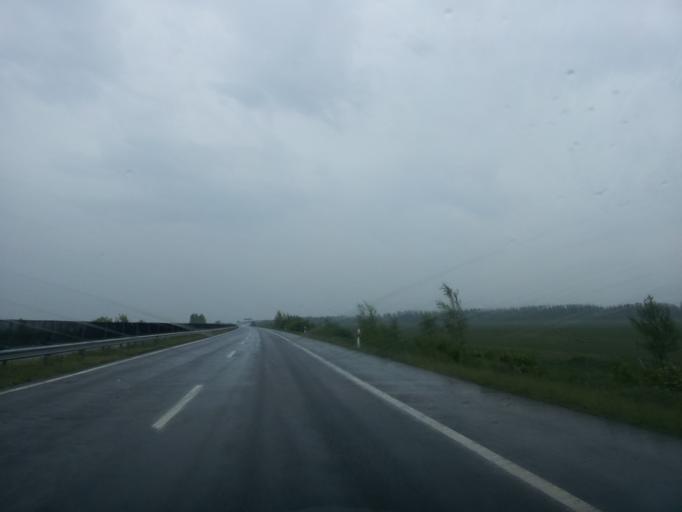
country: HU
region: Tolna
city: Ocseny
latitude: 46.3545
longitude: 18.7563
